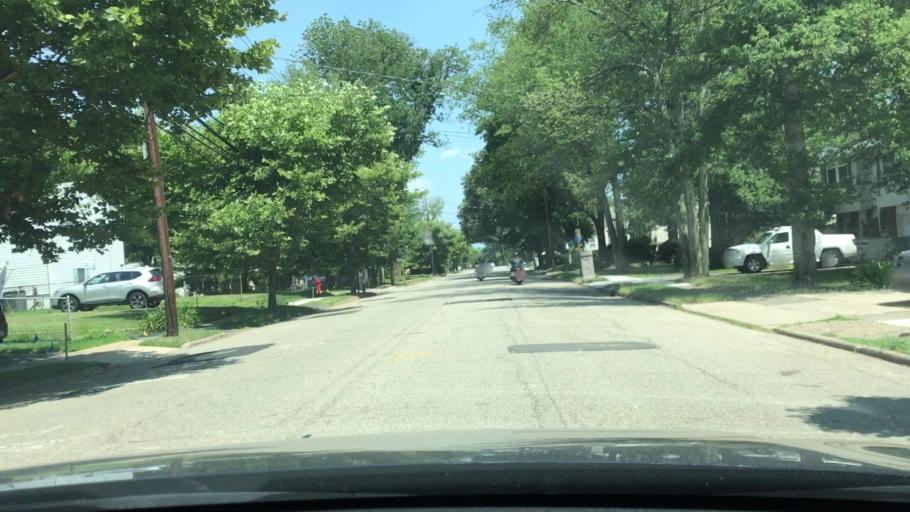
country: US
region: New Jersey
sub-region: Middlesex County
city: Metuchen
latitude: 40.5421
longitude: -74.3776
